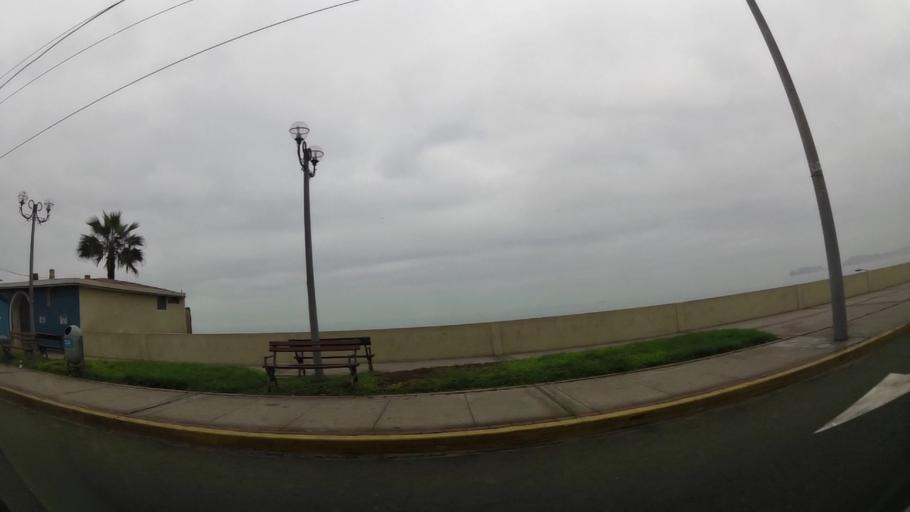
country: PE
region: Lima
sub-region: Lima
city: San Isidro
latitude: -12.0914
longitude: -77.0834
